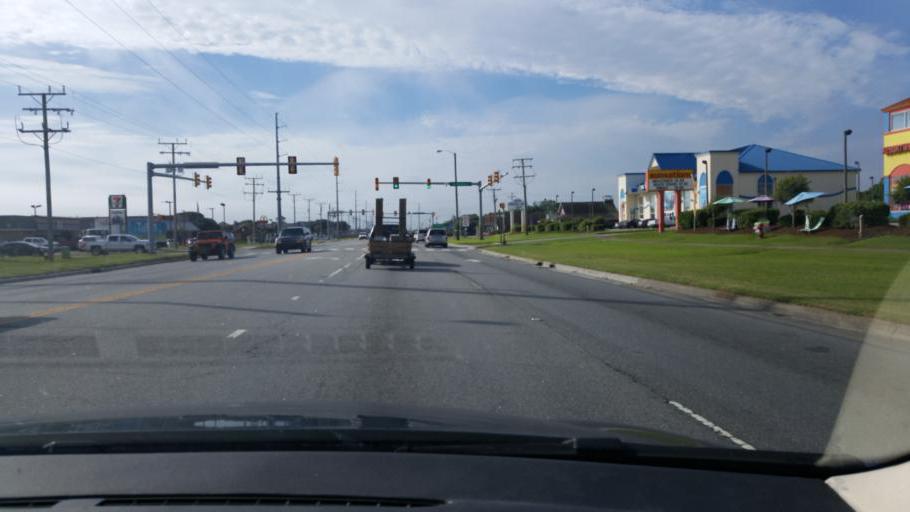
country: US
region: North Carolina
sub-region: Dare County
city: Kill Devil Hills
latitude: 35.9991
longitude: -75.6523
